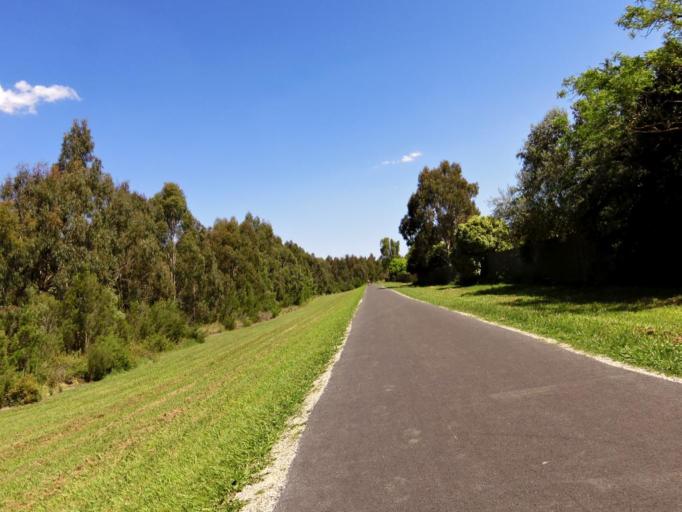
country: AU
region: Victoria
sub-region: Knox
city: Knoxfield
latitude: -37.8970
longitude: 145.2690
